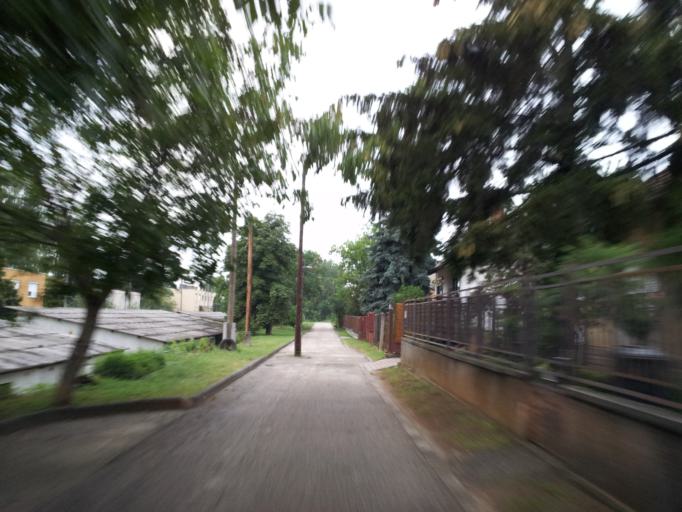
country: HU
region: Tolna
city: Tolna
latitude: 46.4221
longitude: 18.7715
